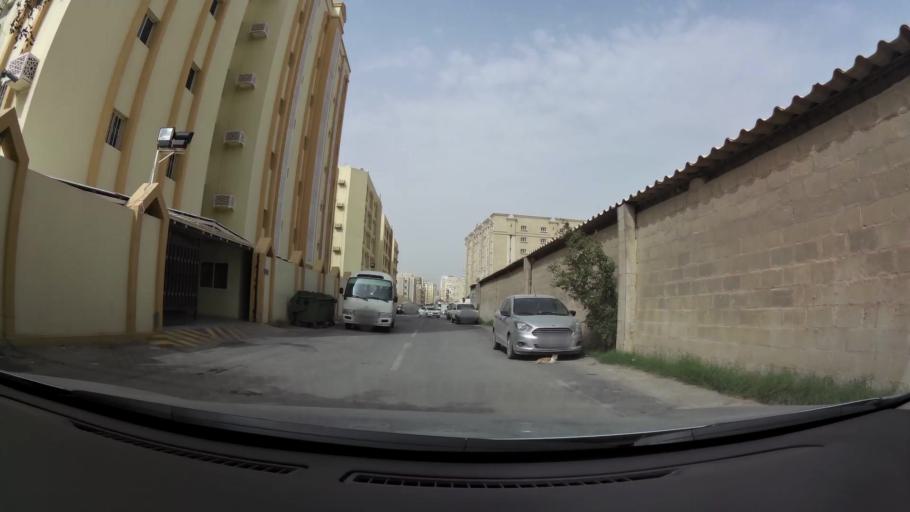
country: QA
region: Baladiyat ad Dawhah
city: Doha
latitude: 25.2723
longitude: 51.5363
